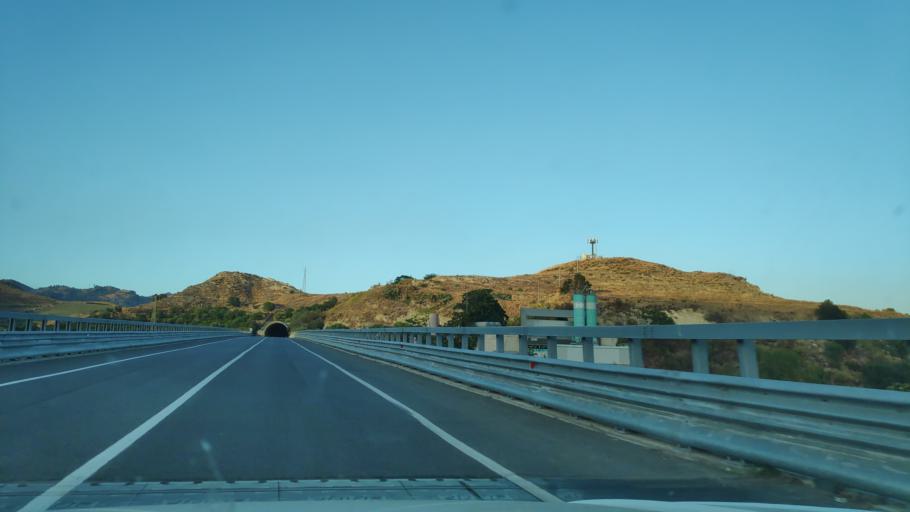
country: IT
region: Calabria
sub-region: Provincia di Reggio Calabria
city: Bova Marina
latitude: 37.9319
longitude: 15.9097
